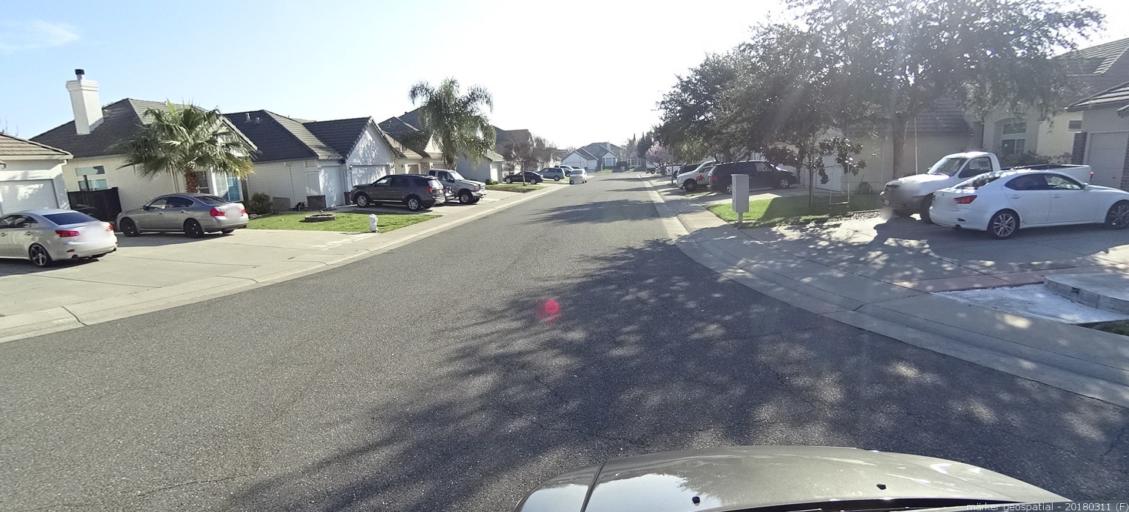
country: US
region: California
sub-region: Sacramento County
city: Vineyard
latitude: 38.4545
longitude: -121.3854
